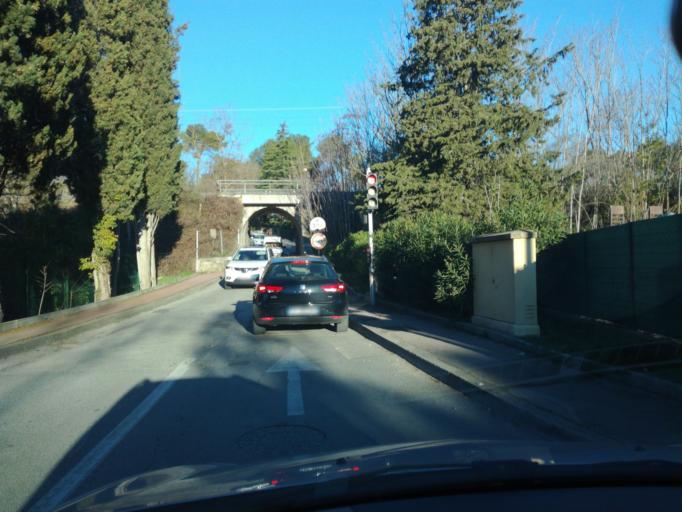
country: FR
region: Provence-Alpes-Cote d'Azur
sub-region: Departement des Alpes-Maritimes
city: Mouans-Sartoux
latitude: 43.6069
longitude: 6.9716
